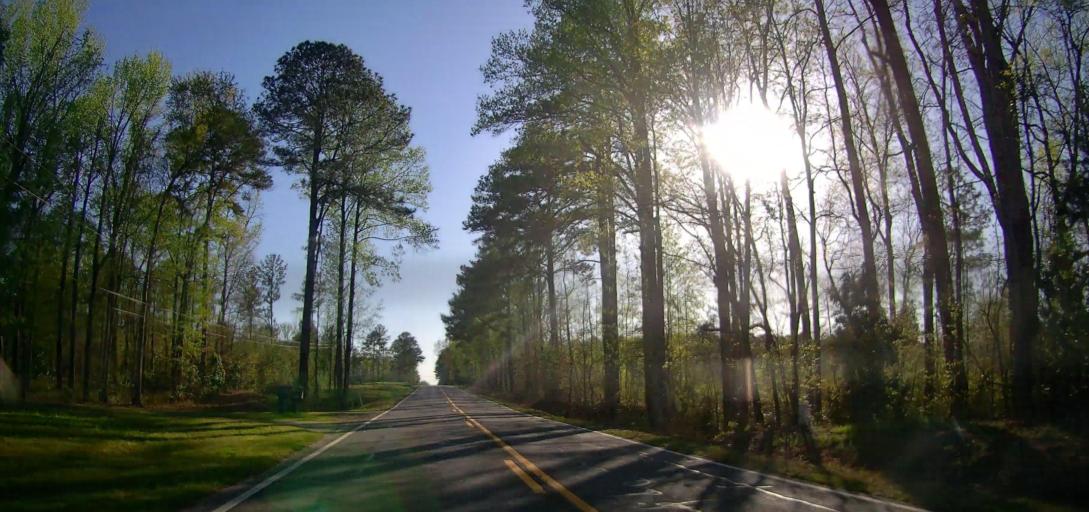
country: US
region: Georgia
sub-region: Butts County
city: Indian Springs
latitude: 33.1968
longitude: -83.9431
